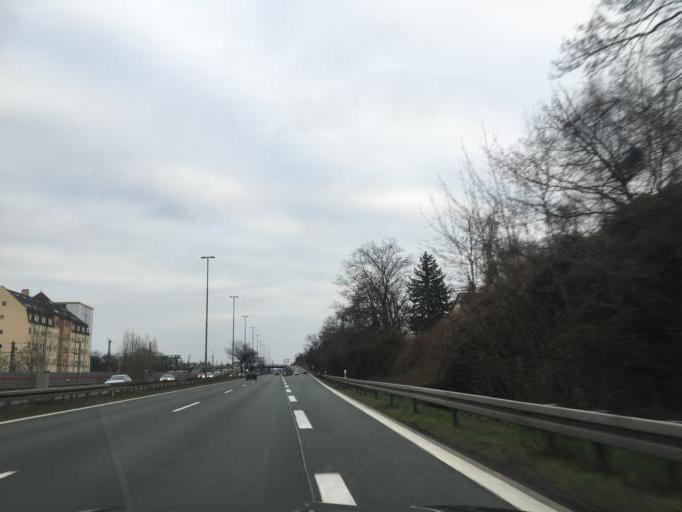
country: DE
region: Bavaria
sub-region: Regierungsbezirk Mittelfranken
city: Wetzendorf
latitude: 49.4540
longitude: 11.0319
